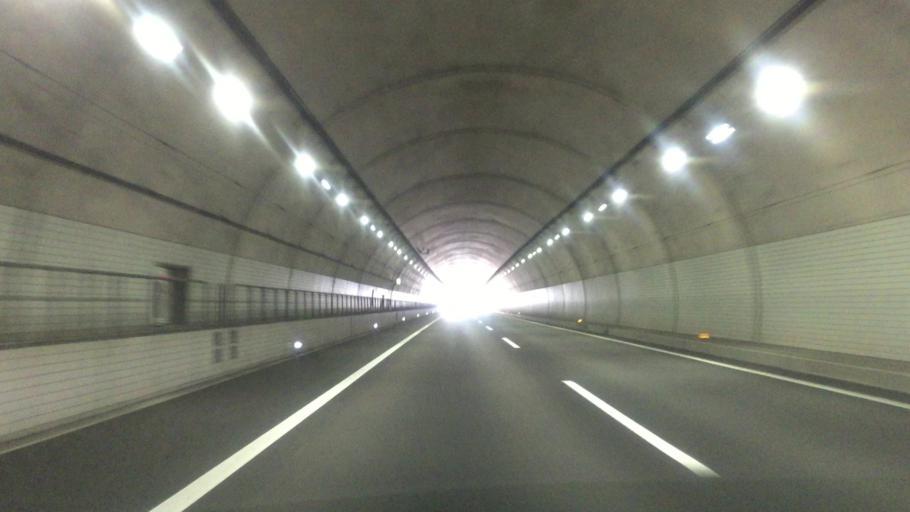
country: JP
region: Aichi
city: Okazaki
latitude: 34.9407
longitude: 137.2591
